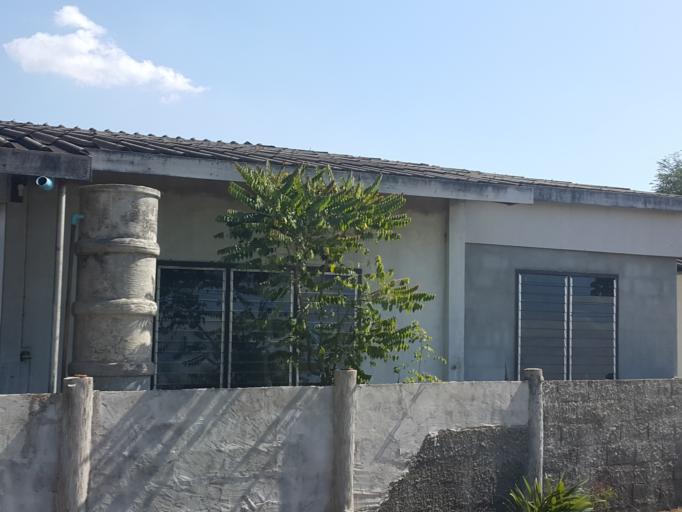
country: TH
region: Chiang Mai
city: Mae Taeng
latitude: 19.0953
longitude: 98.9441
